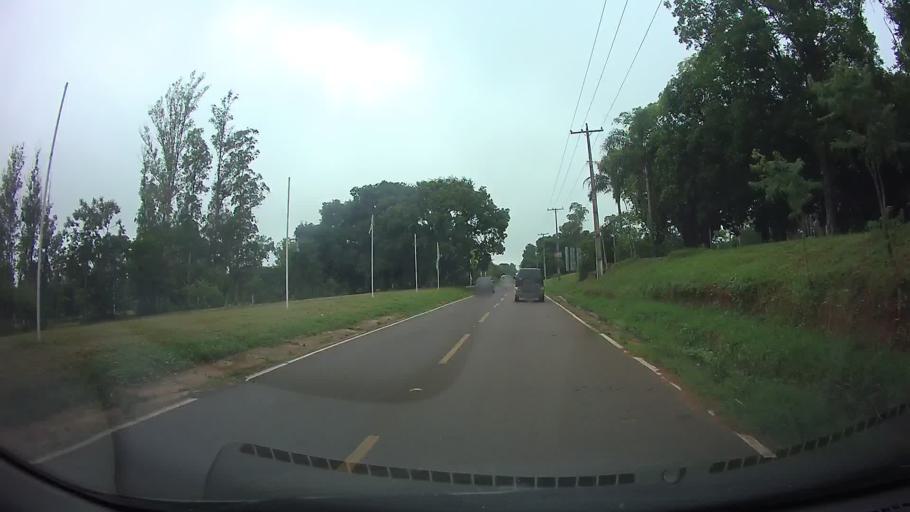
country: PY
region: Central
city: Itaugua
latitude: -25.3616
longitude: -57.3457
